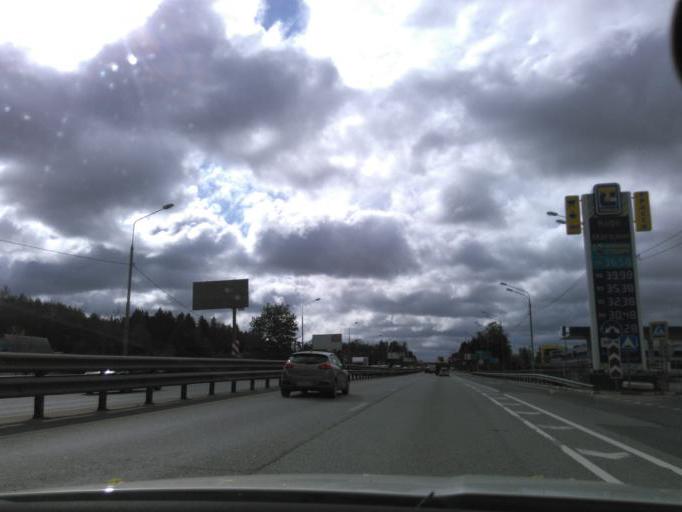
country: RU
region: Moskovskaya
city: Skhodnya
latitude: 55.9721
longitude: 37.3181
